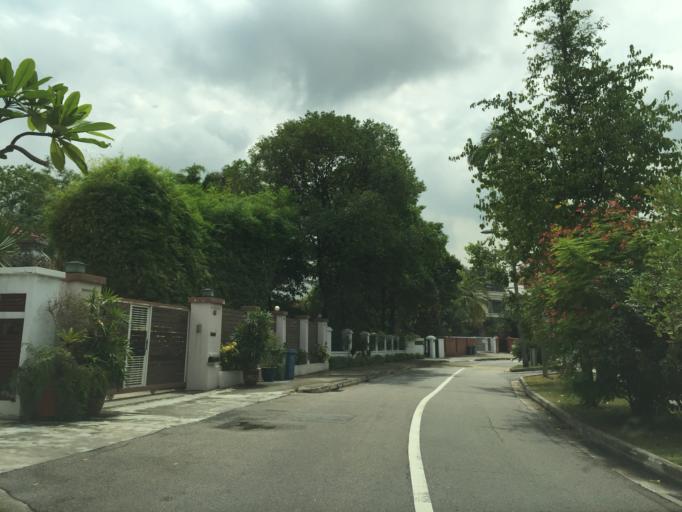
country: SG
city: Singapore
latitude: 1.3192
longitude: 103.8383
